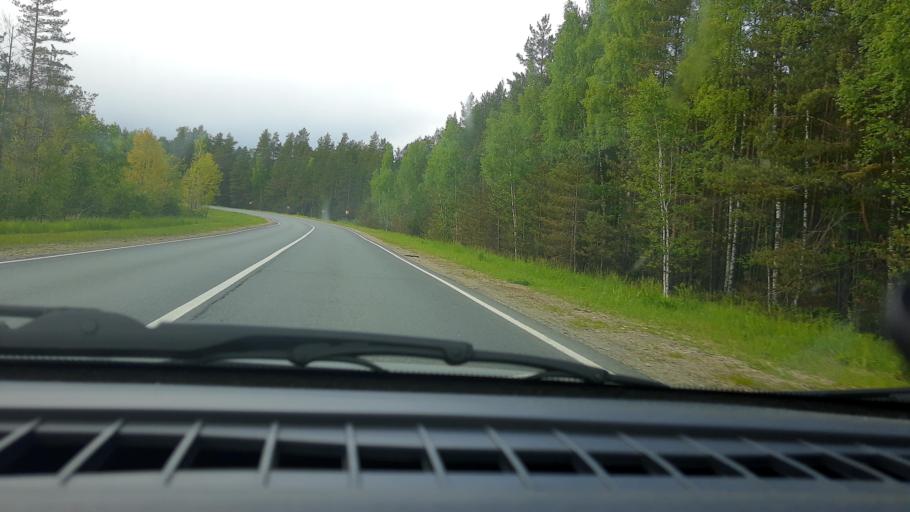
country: RU
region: Nizjnij Novgorod
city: Krasnyye Baki
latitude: 57.1783
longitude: 45.3375
